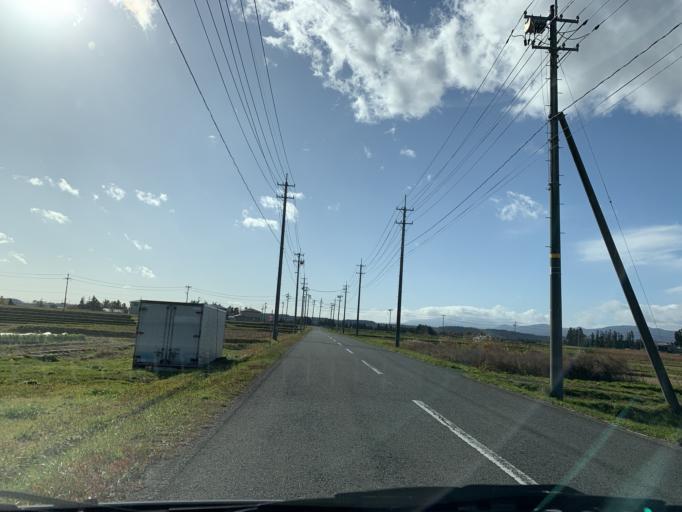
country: JP
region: Iwate
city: Mizusawa
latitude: 39.0584
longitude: 141.1169
